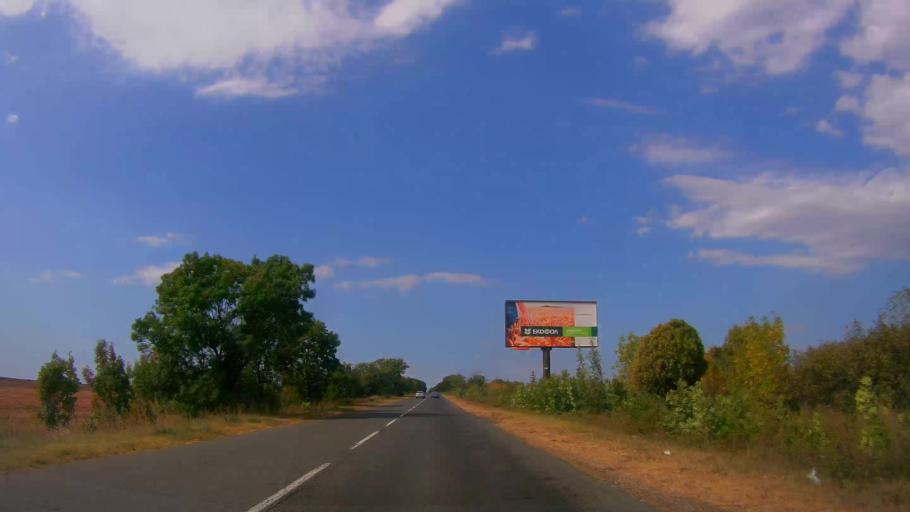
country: BG
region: Burgas
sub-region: Obshtina Aytos
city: Aytos
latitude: 42.6880
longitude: 27.1494
